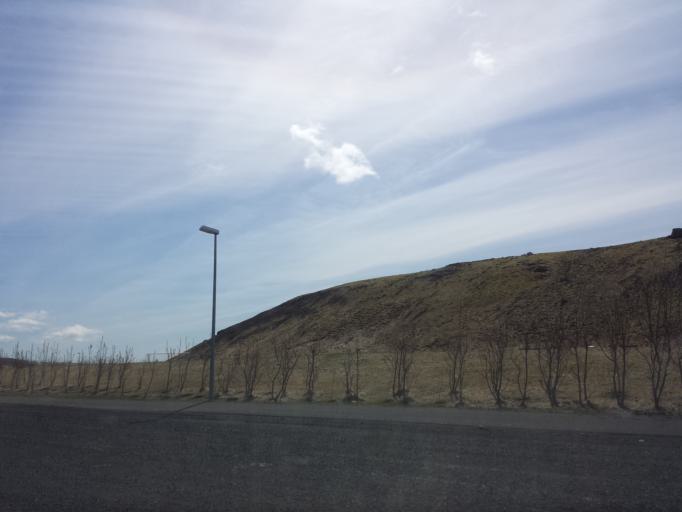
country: IS
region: South
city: Hveragerdi
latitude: 64.0108
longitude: -21.1923
